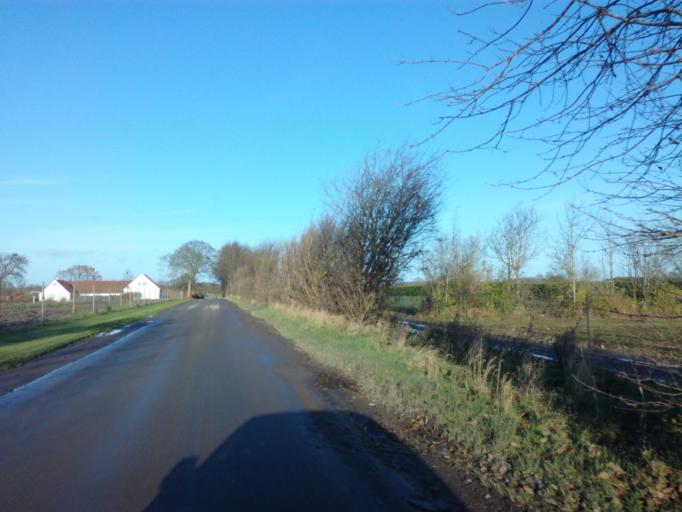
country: DK
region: South Denmark
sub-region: Vejle Kommune
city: Borkop
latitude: 55.6243
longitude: 9.6767
